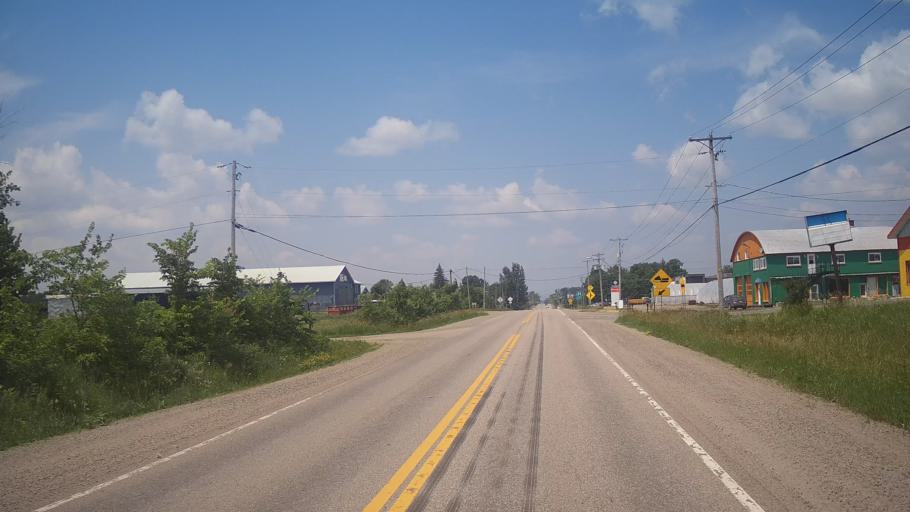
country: CA
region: Quebec
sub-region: Outaouais
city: Shawville
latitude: 45.5964
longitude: -76.4850
